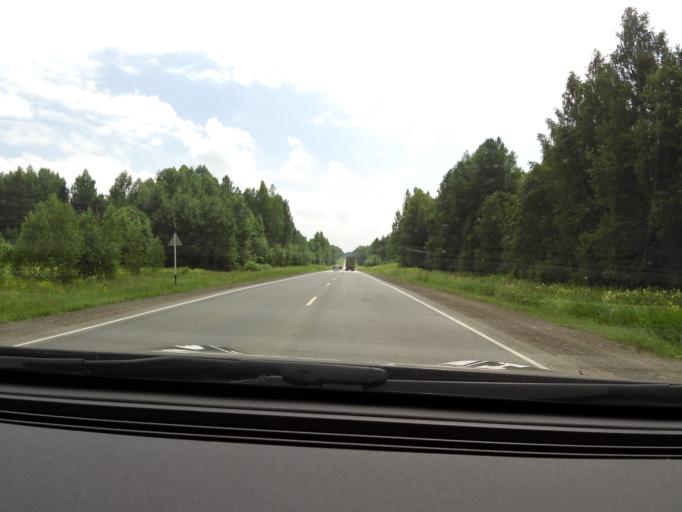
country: RU
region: Perm
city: Kukushtan
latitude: 57.5655
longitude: 56.5685
